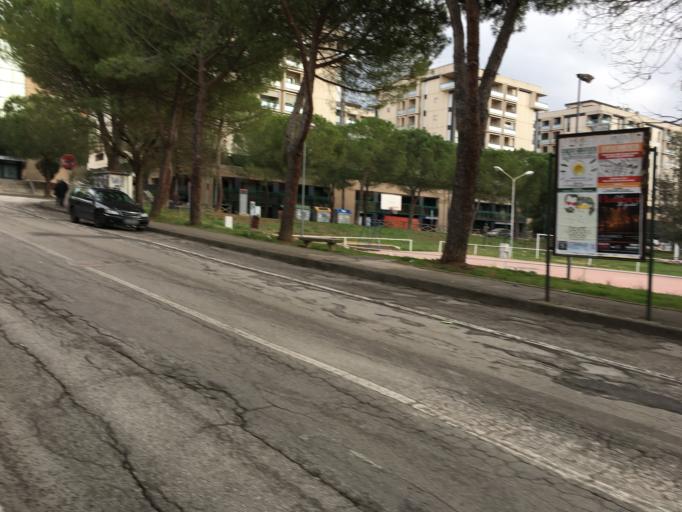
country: IT
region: Umbria
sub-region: Provincia di Perugia
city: Perugia
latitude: 43.1010
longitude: 12.3724
